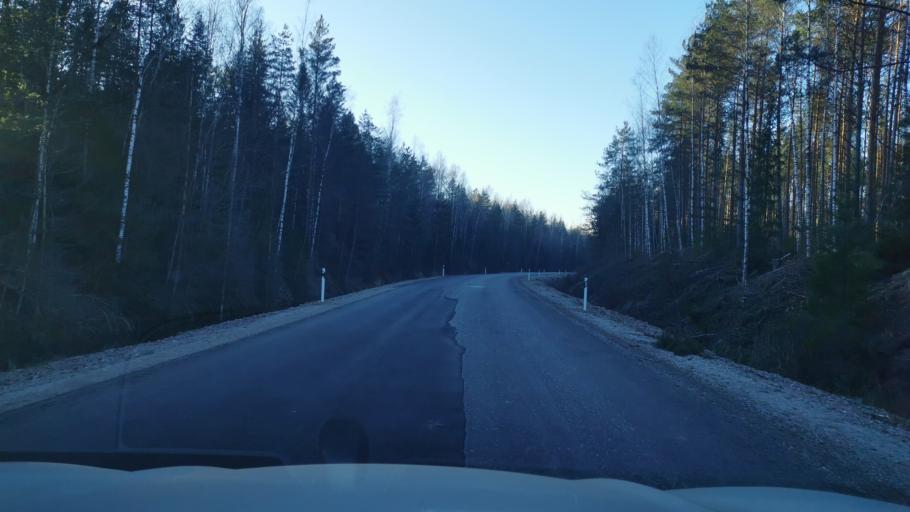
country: EE
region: Ida-Virumaa
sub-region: Kohtla-Nomme vald
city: Kohtla-Nomme
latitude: 59.3442
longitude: 27.1493
